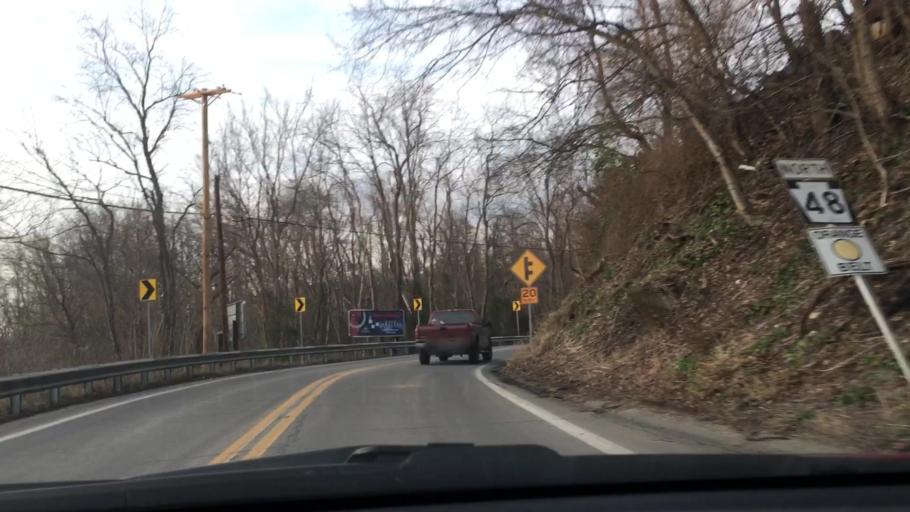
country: US
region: Pennsylvania
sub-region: Allegheny County
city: Versailles
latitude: 40.2840
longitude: -79.8377
